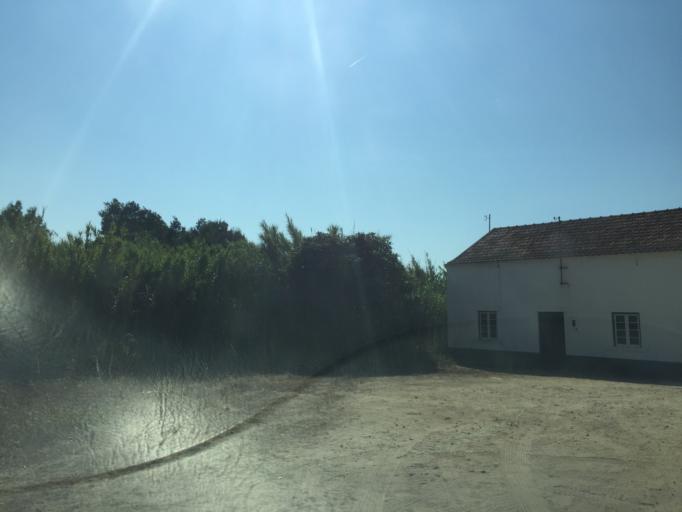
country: PT
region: Coimbra
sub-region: Figueira da Foz
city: Tavarede
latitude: 40.2272
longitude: -8.8510
